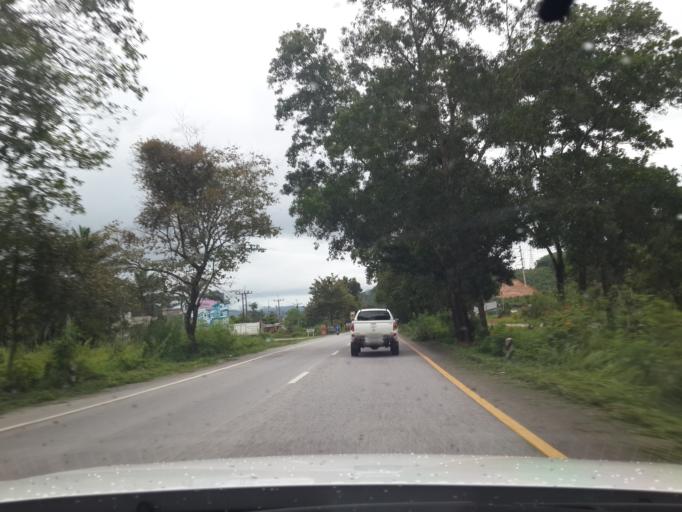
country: TH
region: Songkhla
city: Hat Yai
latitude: 6.9697
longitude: 100.4982
